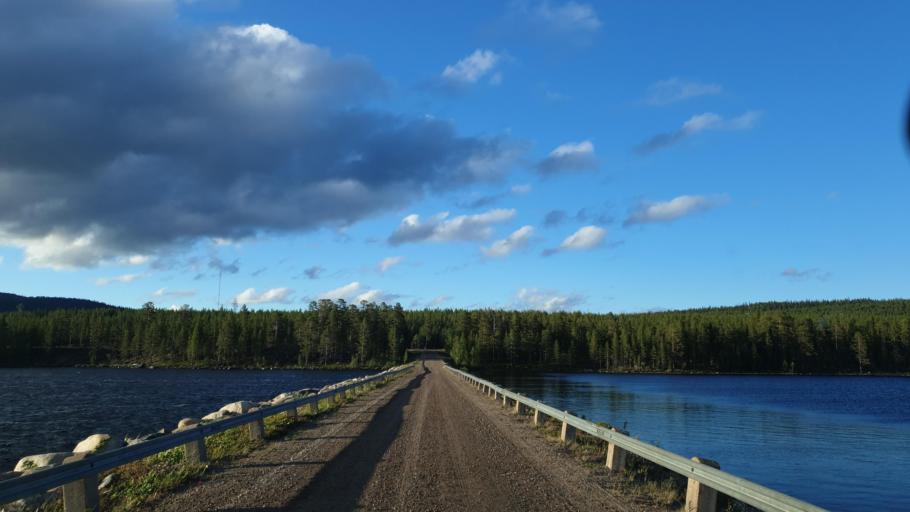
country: SE
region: Norrbotten
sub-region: Arvidsjaurs Kommun
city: Arvidsjaur
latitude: 65.7115
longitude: 18.7095
